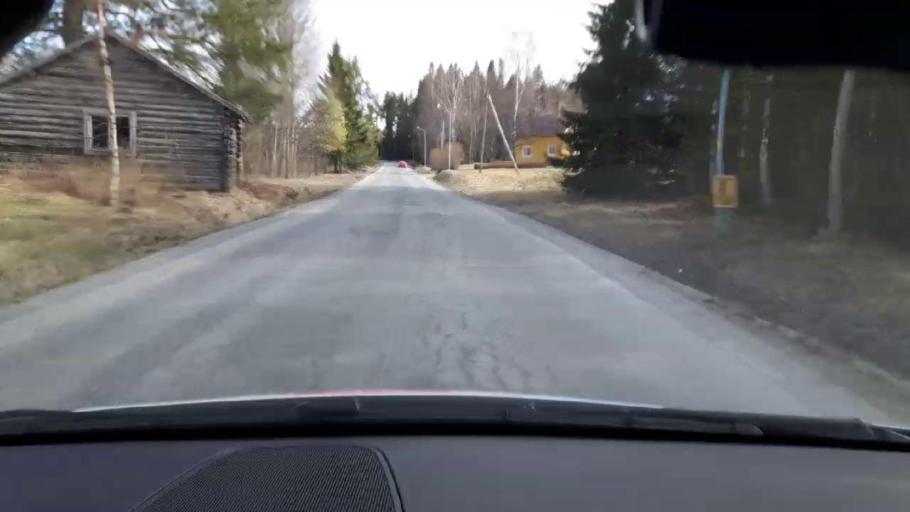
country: SE
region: Jaemtland
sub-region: Bergs Kommun
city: Hoverberg
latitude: 62.7909
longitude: 14.4848
